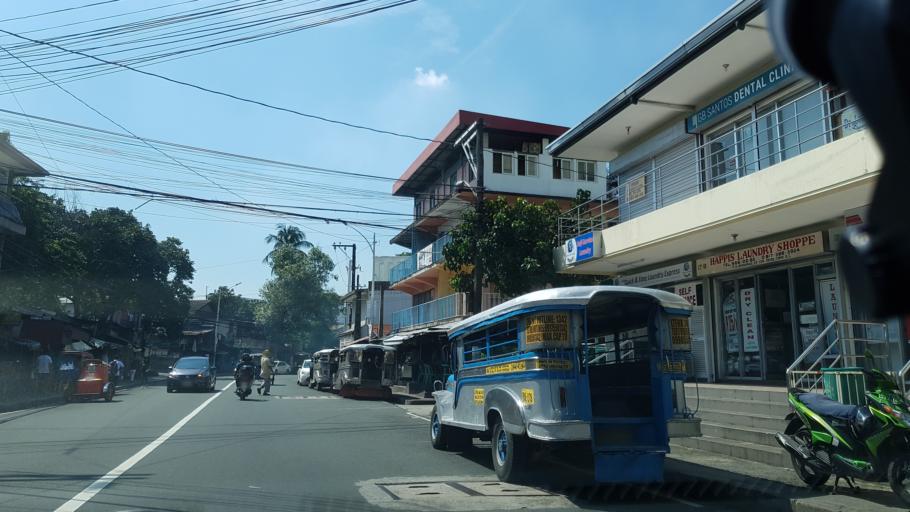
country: PH
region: Metro Manila
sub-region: San Juan
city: San Juan
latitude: 14.6195
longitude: 121.0482
